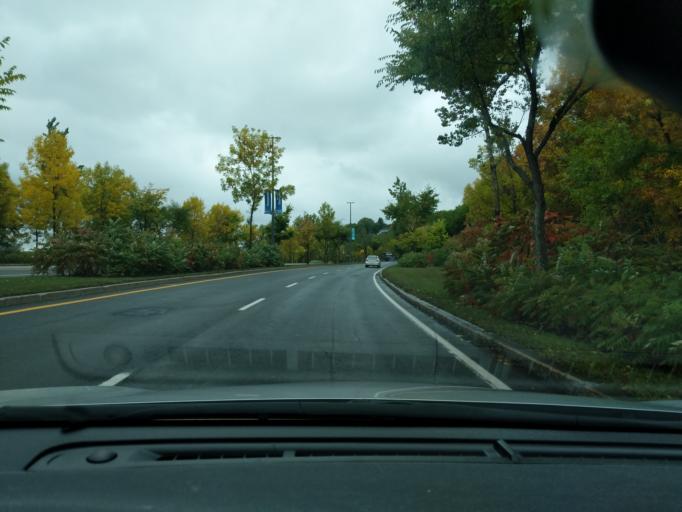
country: CA
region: Quebec
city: Quebec
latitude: 46.7595
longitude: -71.2675
